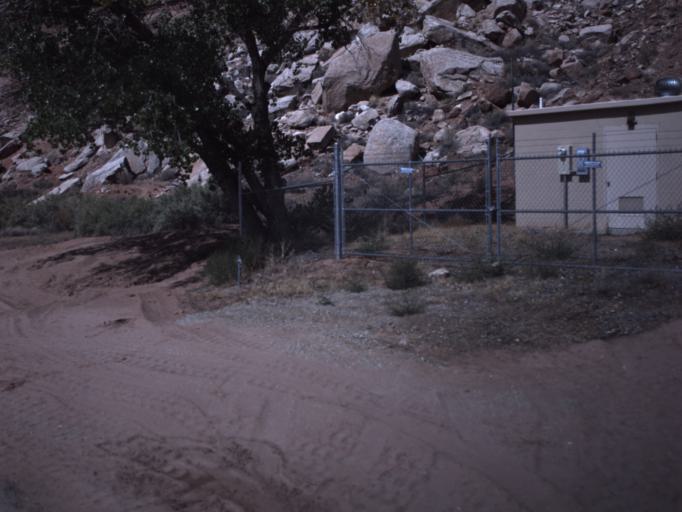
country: US
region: Utah
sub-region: San Juan County
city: Blanding
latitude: 37.2845
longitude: -109.5339
